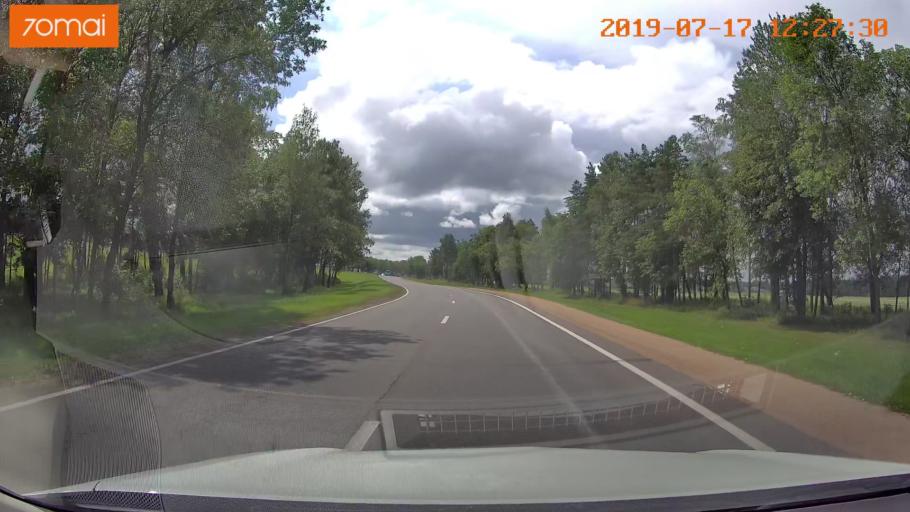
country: BY
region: Minsk
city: Borovlyany
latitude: 53.9764
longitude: 27.6498
